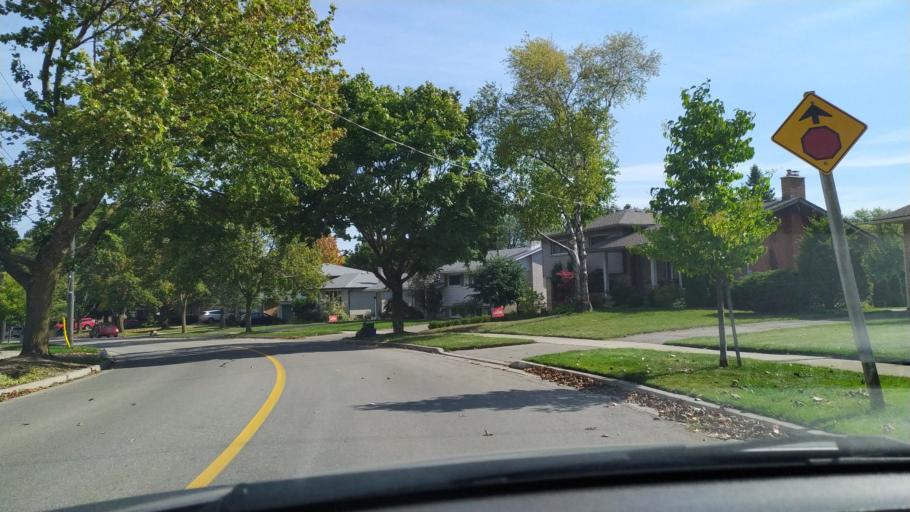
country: CA
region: Ontario
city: Kitchener
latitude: 43.4280
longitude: -80.5136
